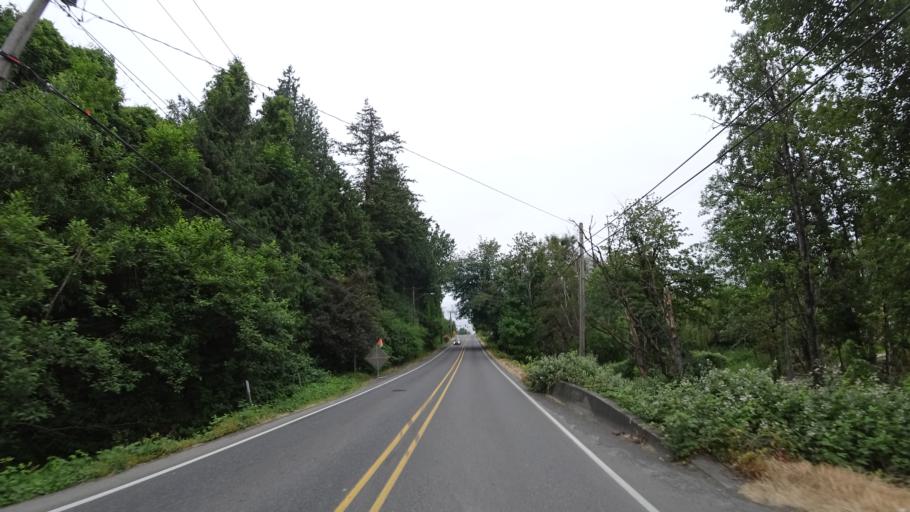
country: US
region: Oregon
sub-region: Multnomah County
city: Fairview
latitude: 45.5427
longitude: -122.4296
